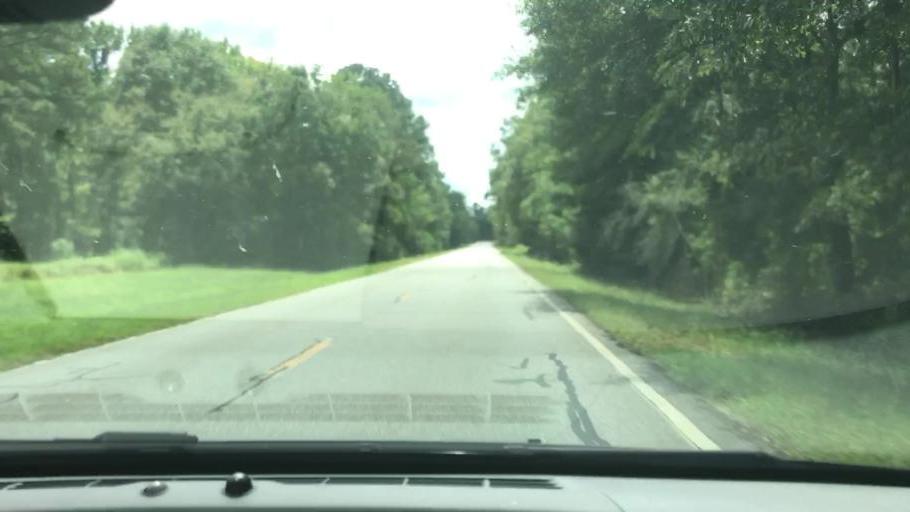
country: US
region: Georgia
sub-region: Quitman County
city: Georgetown
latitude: 32.1019
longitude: -85.0386
